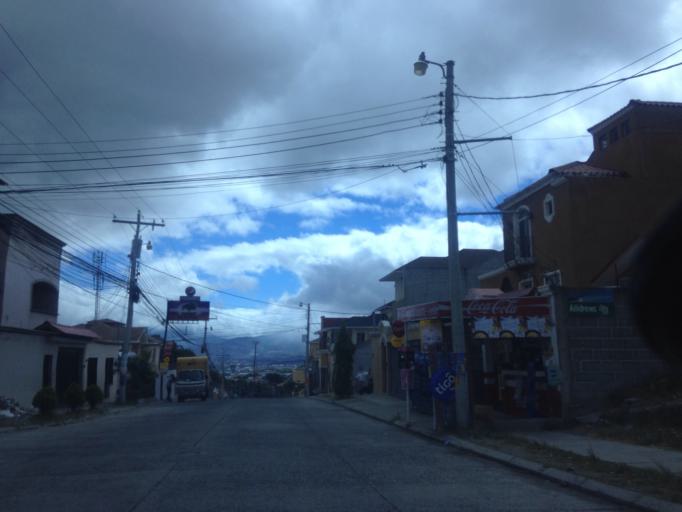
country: HN
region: Francisco Morazan
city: Yaguacire
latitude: 14.0523
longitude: -87.2411
